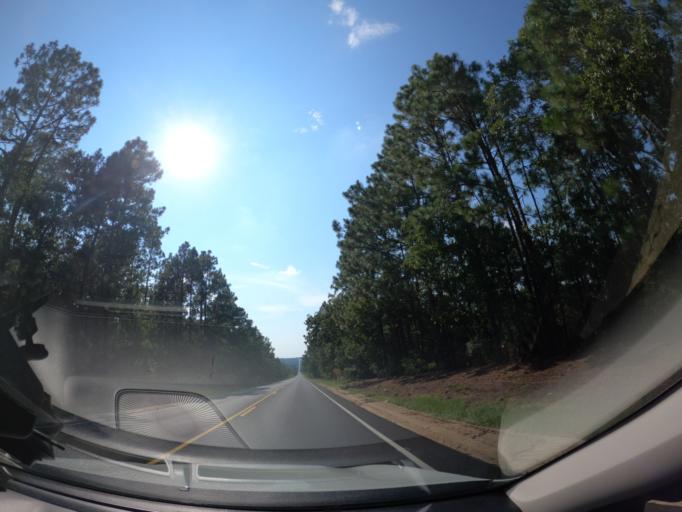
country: US
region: South Carolina
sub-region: Aiken County
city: Jackson
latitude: 33.4042
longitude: -81.7750
